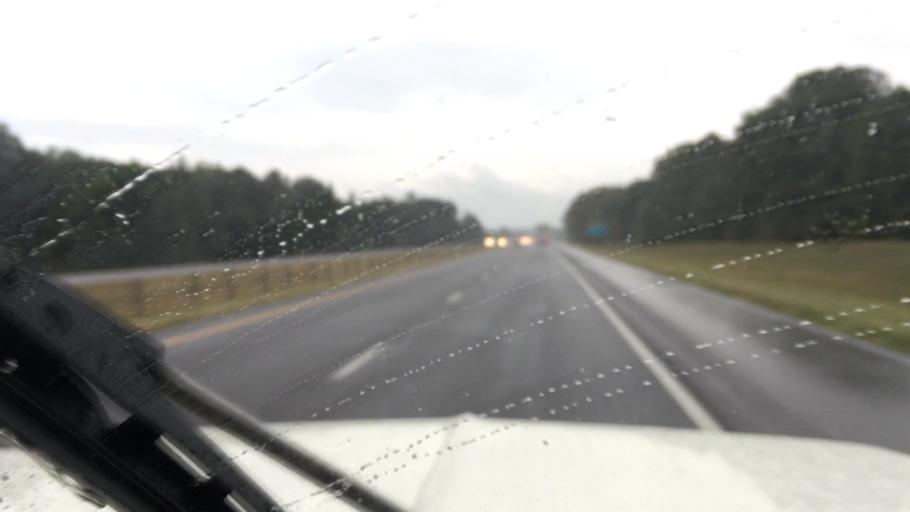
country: US
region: Alabama
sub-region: Morgan County
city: Hartselle
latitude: 34.4230
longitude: -86.8990
